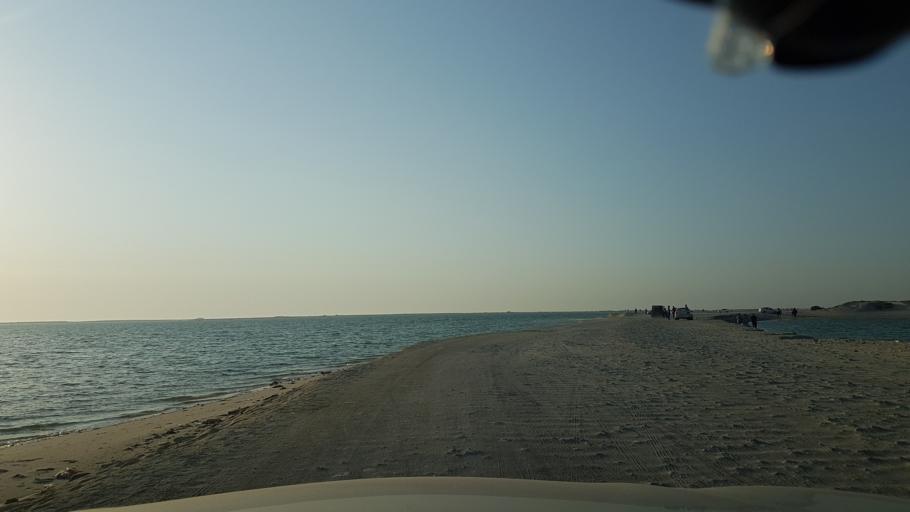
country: BH
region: Manama
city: Jidd Hafs
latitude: 26.2396
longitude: 50.5035
